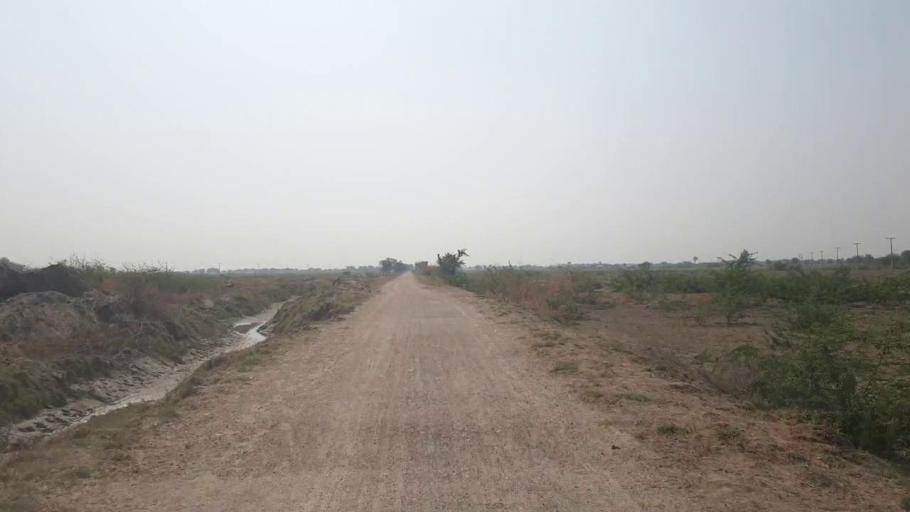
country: PK
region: Sindh
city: Dhoro Naro
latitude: 25.4467
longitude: 69.6252
